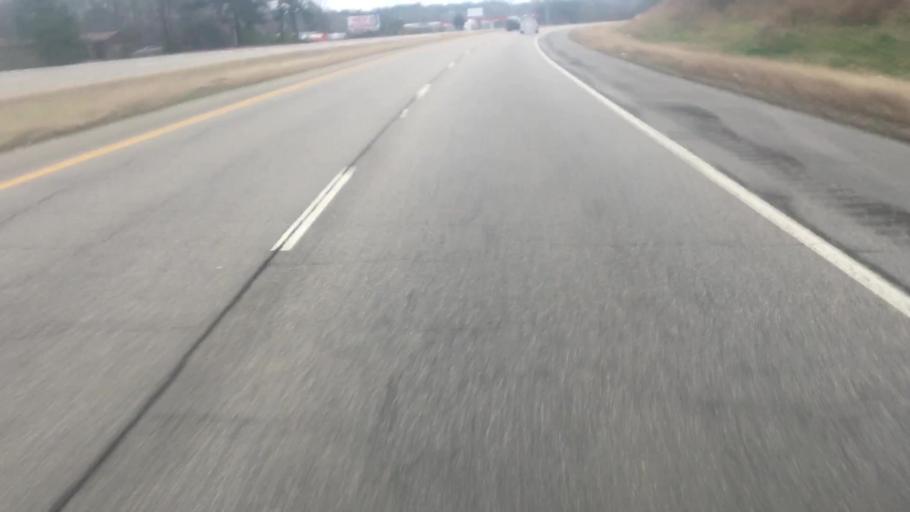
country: US
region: Alabama
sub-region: Walker County
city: Cordova
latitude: 33.8211
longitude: -87.1568
